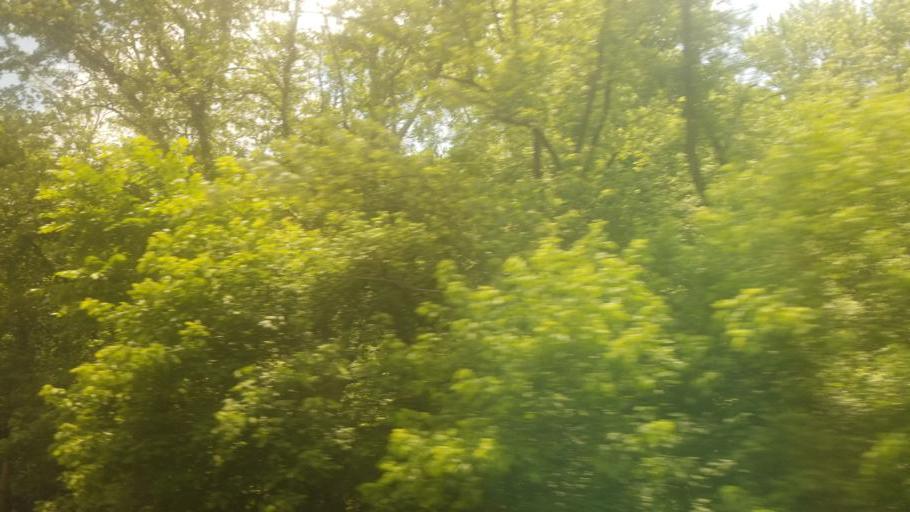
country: US
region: Maryland
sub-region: Frederick County
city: Brunswick
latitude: 39.3207
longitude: -77.6588
